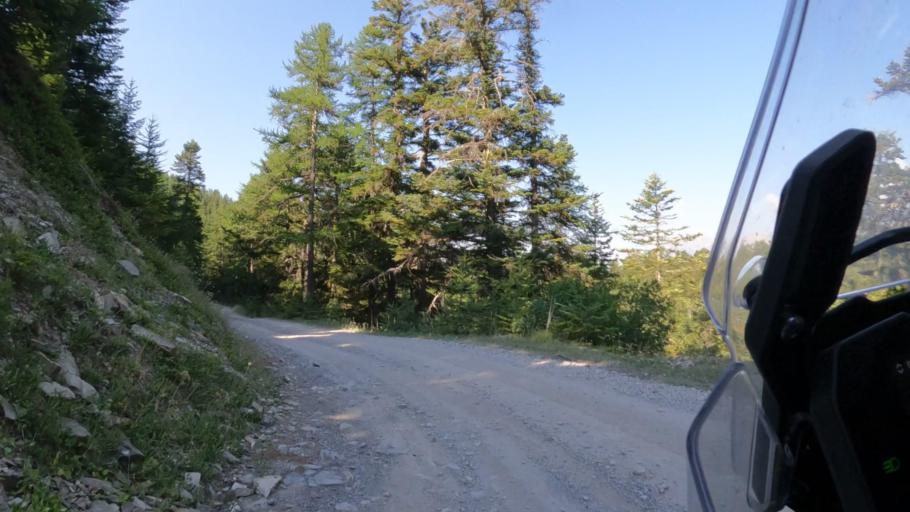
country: FR
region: Provence-Alpes-Cote d'Azur
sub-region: Departement des Hautes-Alpes
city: Embrun
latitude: 44.5947
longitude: 6.5715
